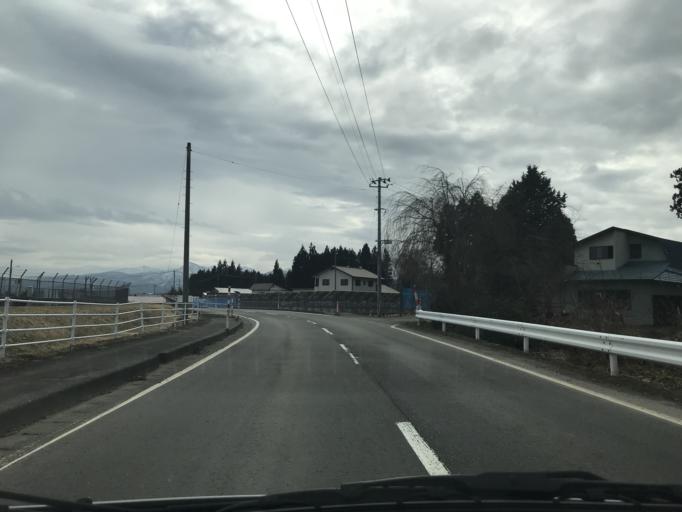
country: JP
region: Iwate
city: Hanamaki
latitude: 39.3506
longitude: 140.9840
